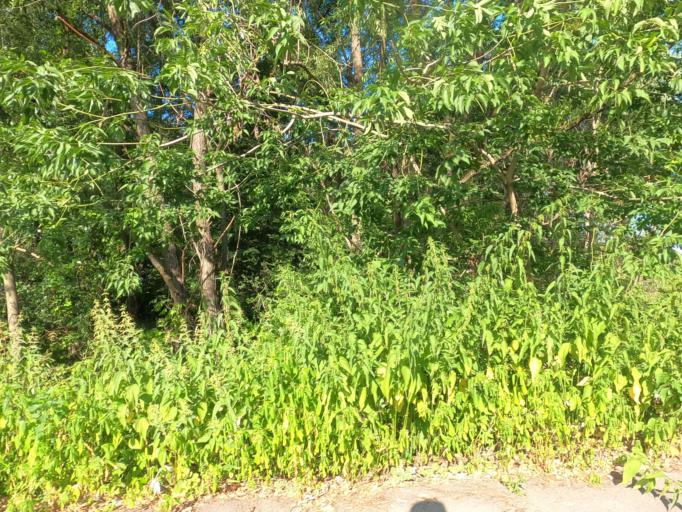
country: RU
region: Moskovskaya
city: Konobeyevo
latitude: 55.4131
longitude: 38.6948
